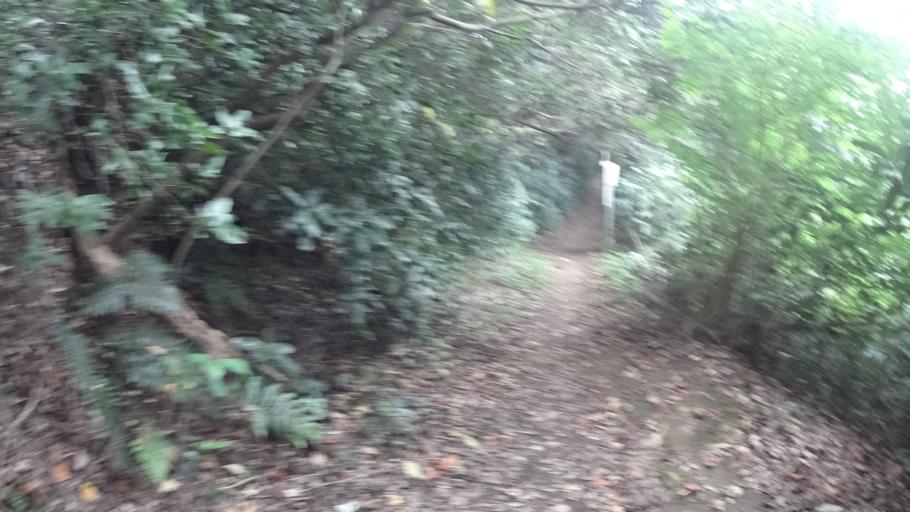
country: JP
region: Kanagawa
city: Zushi
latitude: 35.2906
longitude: 139.6103
